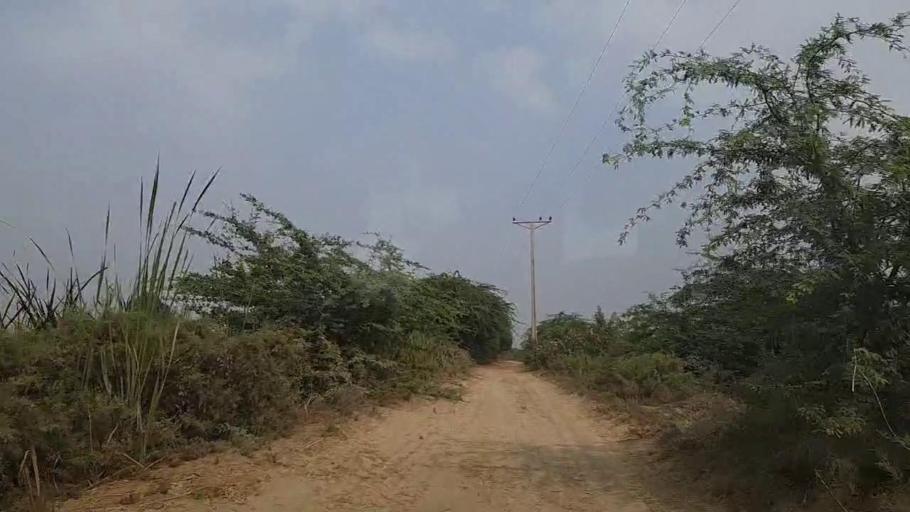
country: PK
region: Sindh
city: Mirpur Sakro
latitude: 24.6124
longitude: 67.7168
